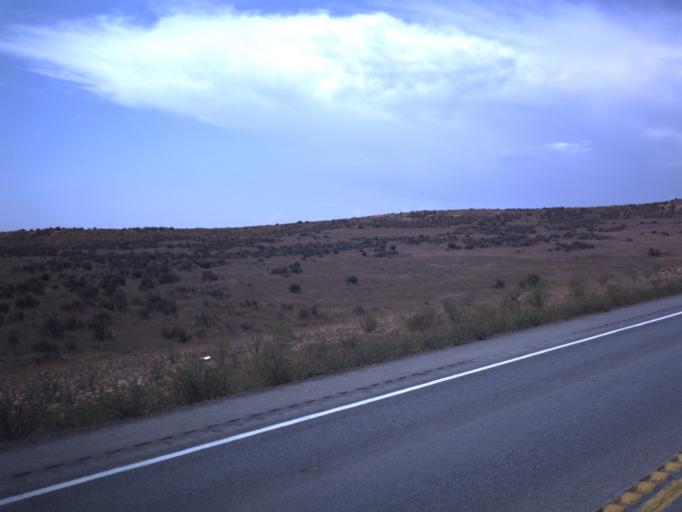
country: US
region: Utah
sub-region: Uintah County
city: Maeser
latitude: 40.3356
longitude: -109.6400
